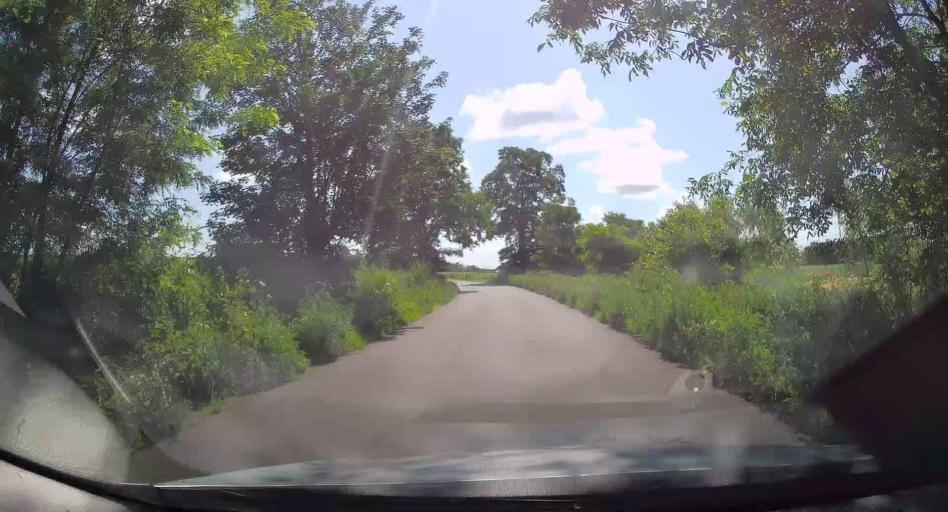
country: PL
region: Subcarpathian Voivodeship
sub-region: Powiat jaroslawski
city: Sosnica
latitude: 49.8676
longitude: 22.8626
